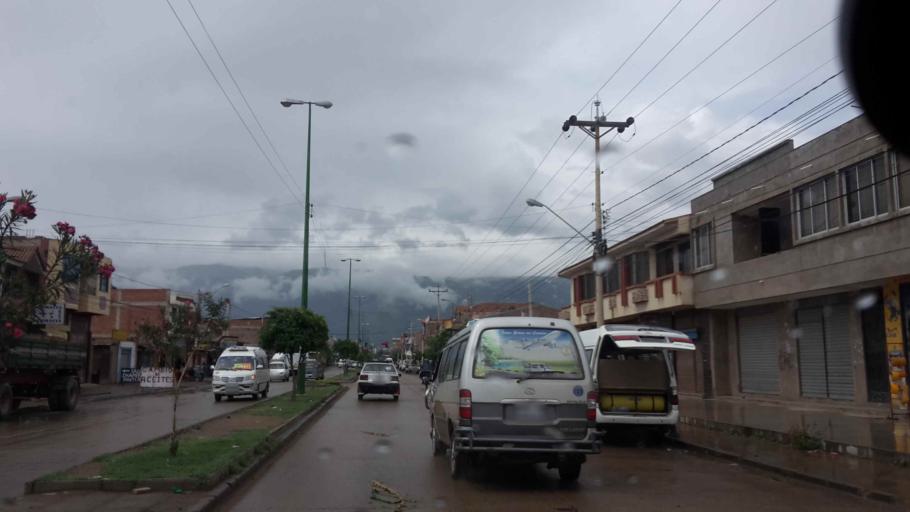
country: BO
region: Cochabamba
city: Cochabamba
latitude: -17.4357
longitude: -66.1614
